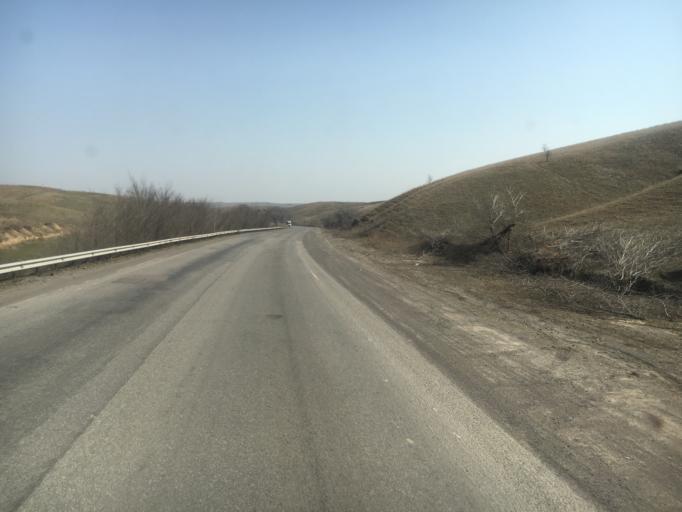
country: KZ
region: Almaty Oblysy
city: Burunday
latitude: 43.2904
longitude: 76.2438
